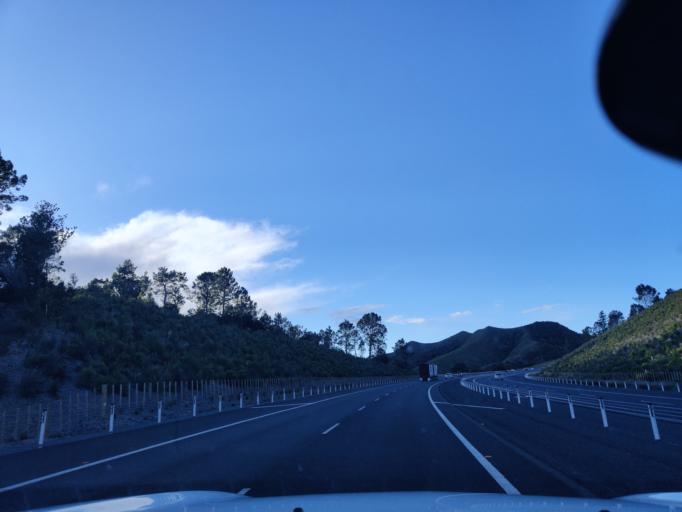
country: NZ
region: Waikato
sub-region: Waikato District
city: Ngaruawahia
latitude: -37.5795
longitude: 175.1855
